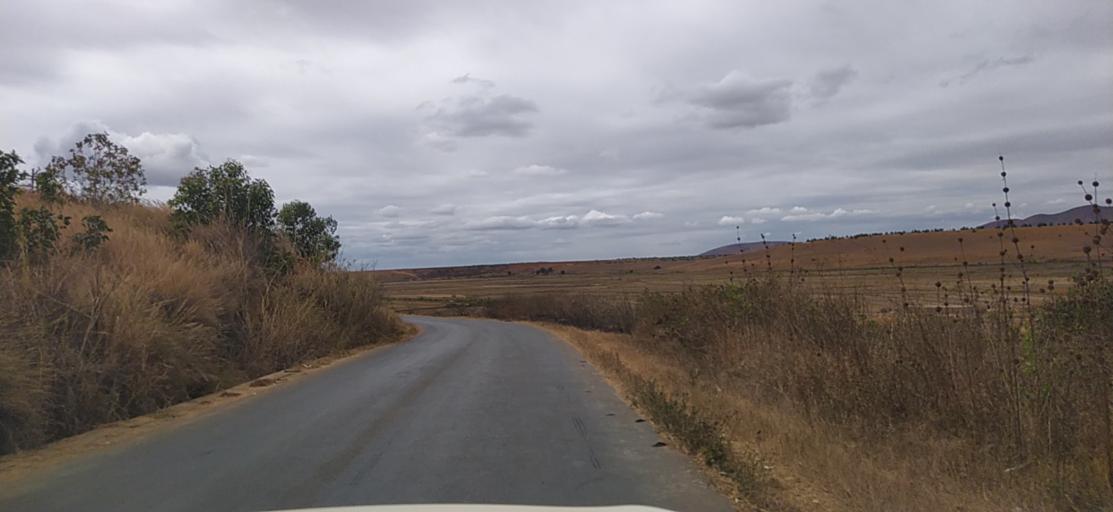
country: MG
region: Alaotra Mangoro
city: Ambatondrazaka
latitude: -17.9262
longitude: 48.2580
